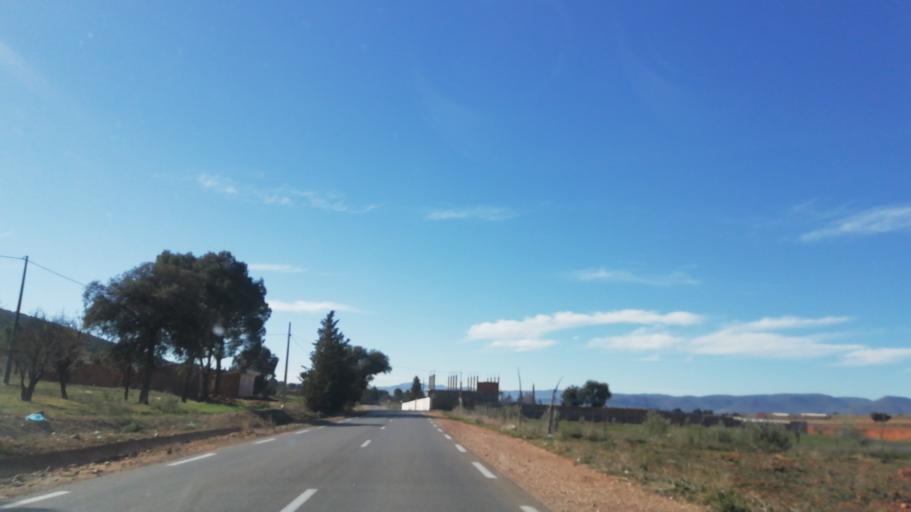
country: DZ
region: Tlemcen
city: Sebdou
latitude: 34.6859
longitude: -1.2491
